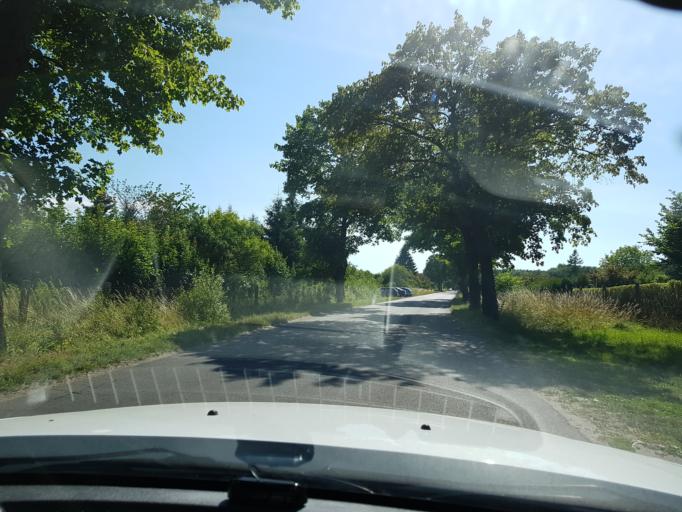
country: PL
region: West Pomeranian Voivodeship
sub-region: Powiat bialogardzki
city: Bialogard
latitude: 53.9992
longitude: 15.9723
